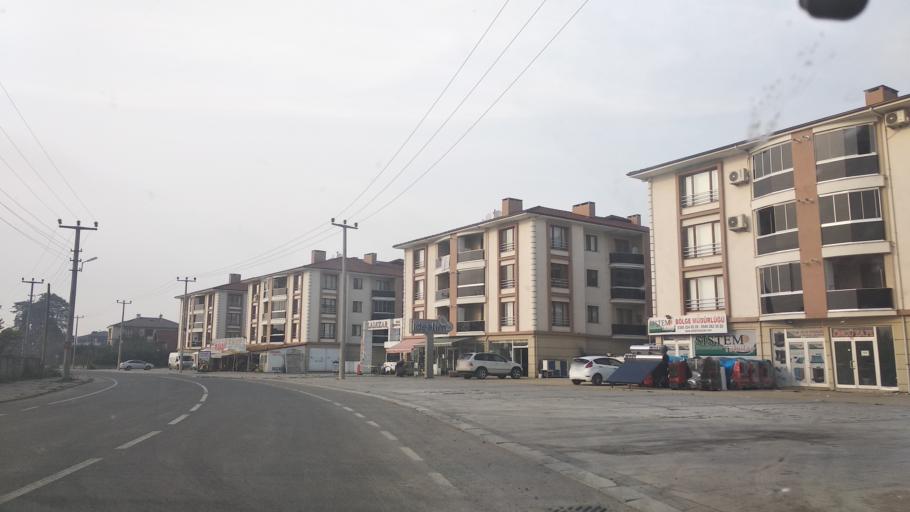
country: TR
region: Duzce
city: Duzce
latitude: 40.8301
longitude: 31.1716
